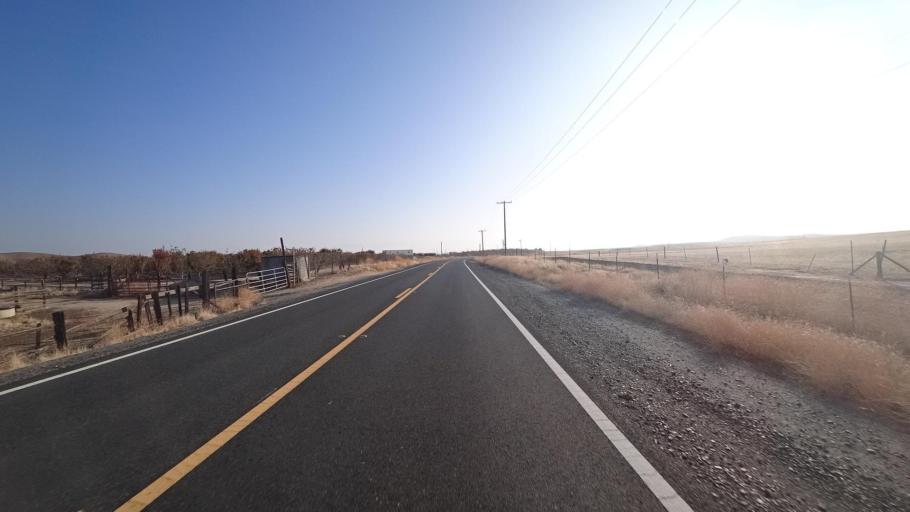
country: US
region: California
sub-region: Tulare County
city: Richgrove
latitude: 35.7620
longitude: -119.0367
